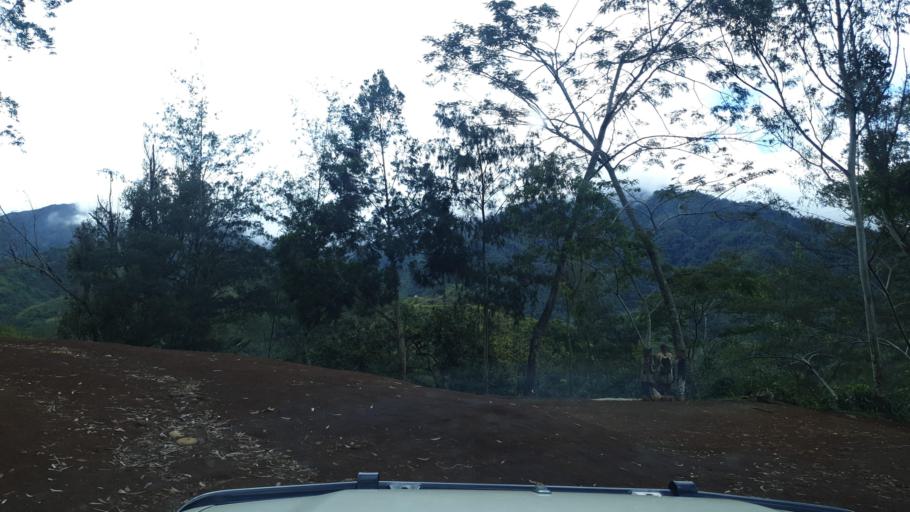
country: PG
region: Eastern Highlands
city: Goroka
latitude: -5.9179
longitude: 145.2575
